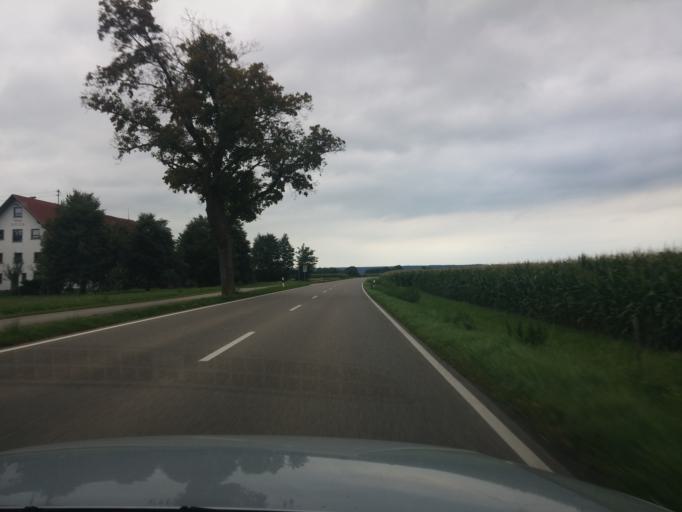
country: DE
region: Bavaria
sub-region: Swabia
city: Buxheim
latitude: 47.9622
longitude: 10.1322
